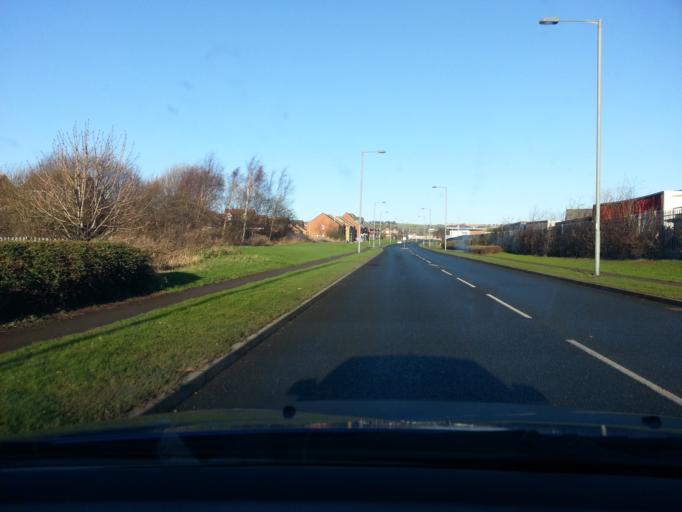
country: GB
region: England
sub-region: County Durham
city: Crook
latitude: 54.7086
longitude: -1.7518
